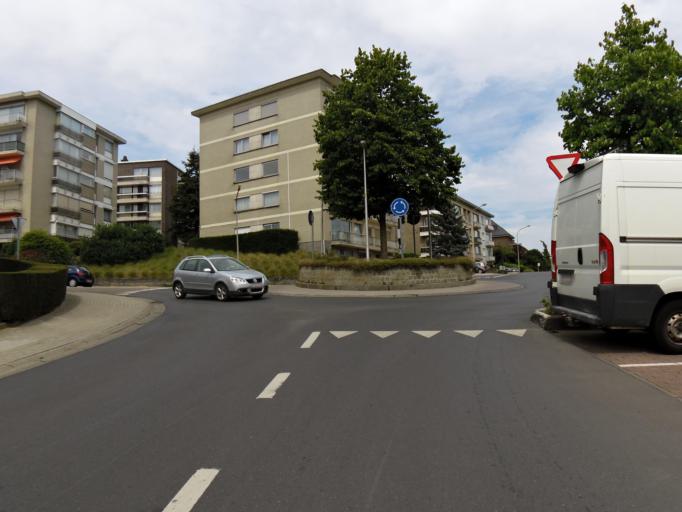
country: BE
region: Flanders
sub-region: Provincie Vlaams-Brabant
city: Dilbeek
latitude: 50.8415
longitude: 4.2585
